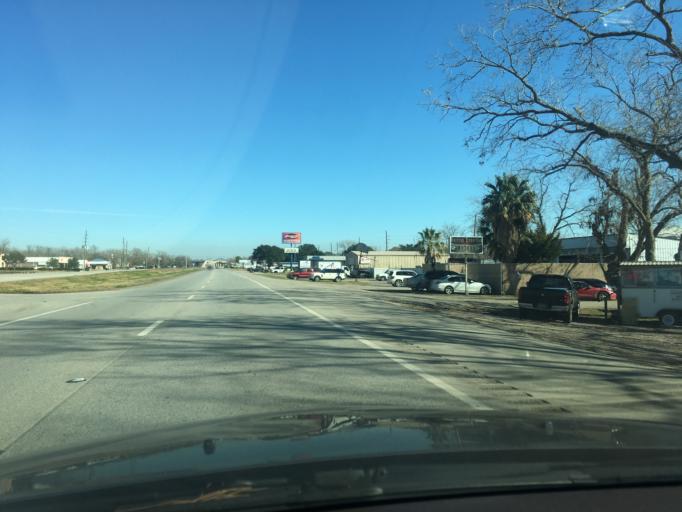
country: US
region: Texas
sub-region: Fort Bend County
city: Richmond
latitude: 29.5867
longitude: -95.7511
